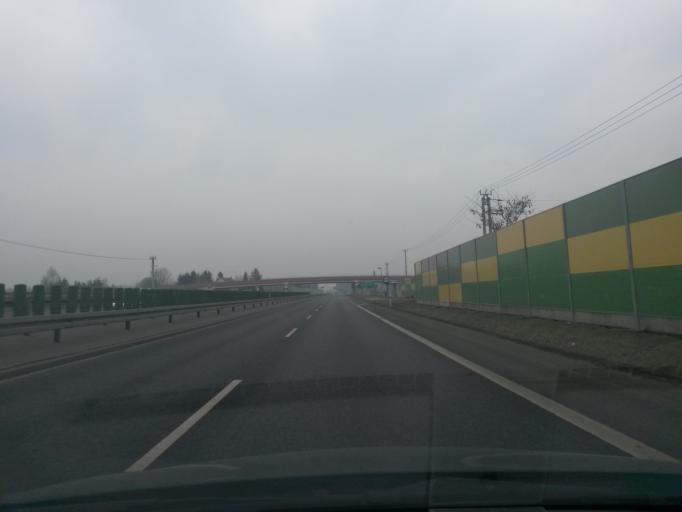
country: PL
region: Masovian Voivodeship
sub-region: Powiat legionowski
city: Serock
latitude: 52.4815
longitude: 21.0389
